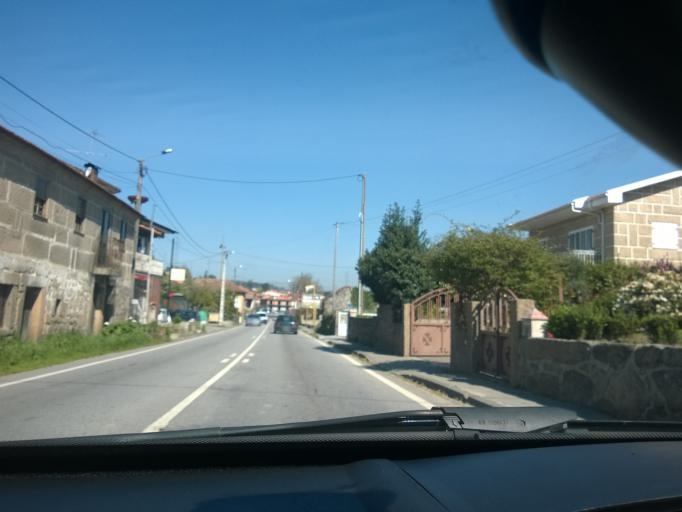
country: PT
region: Porto
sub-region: Paredes
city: Paredes
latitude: 41.1727
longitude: -8.3056
